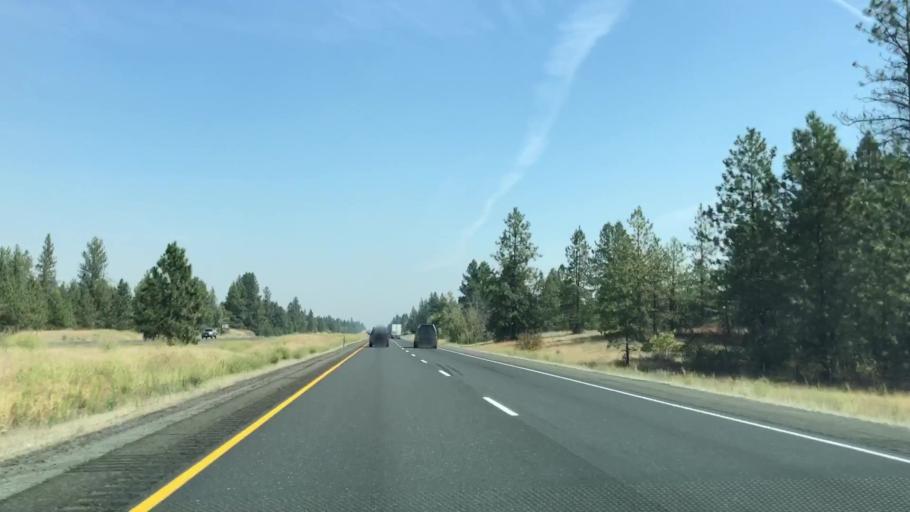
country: US
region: Washington
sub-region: Spokane County
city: Medical Lake
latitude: 47.4672
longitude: -117.7516
